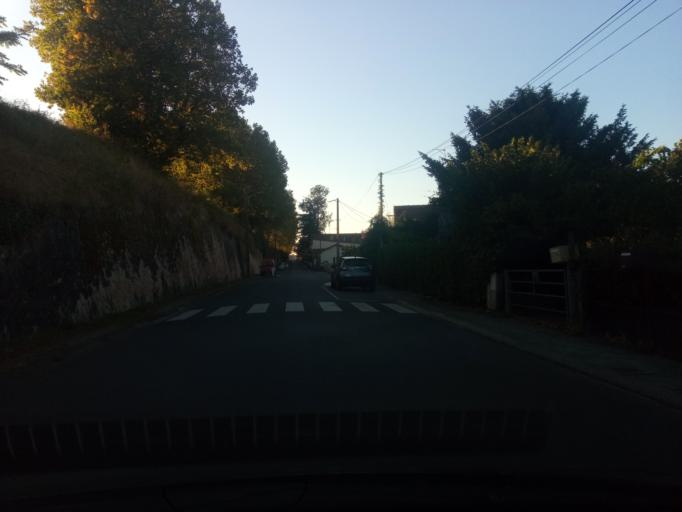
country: FR
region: Poitou-Charentes
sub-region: Departement de la Vienne
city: Montmorillon
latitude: 46.4154
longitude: 0.8774
